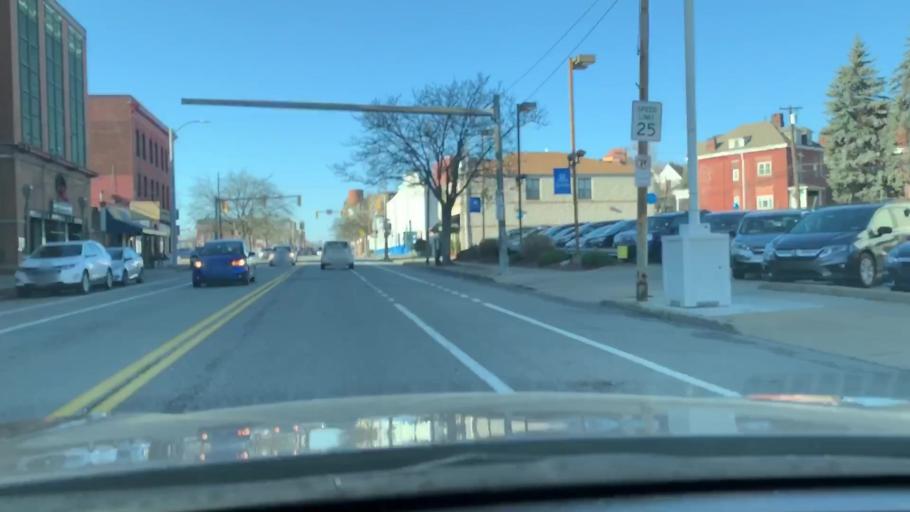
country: US
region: Pennsylvania
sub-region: Allegheny County
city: Bloomfield
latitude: 40.4584
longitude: -79.9430
